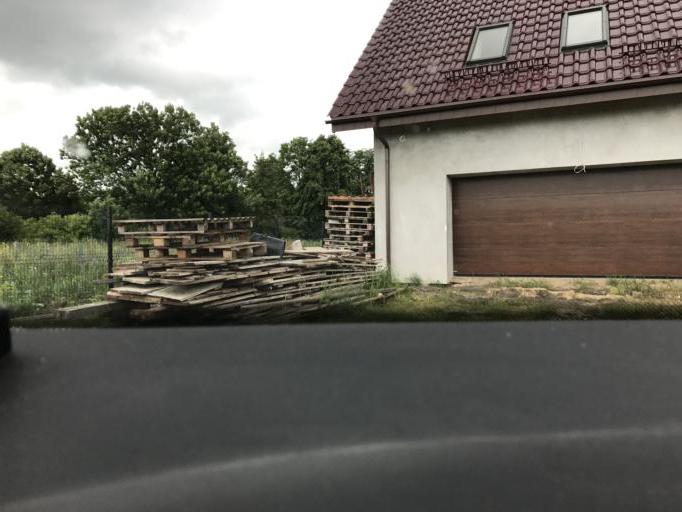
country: PL
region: Pomeranian Voivodeship
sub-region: Powiat gdanski
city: Pruszcz Gdanski
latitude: 54.2816
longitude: 18.6497
